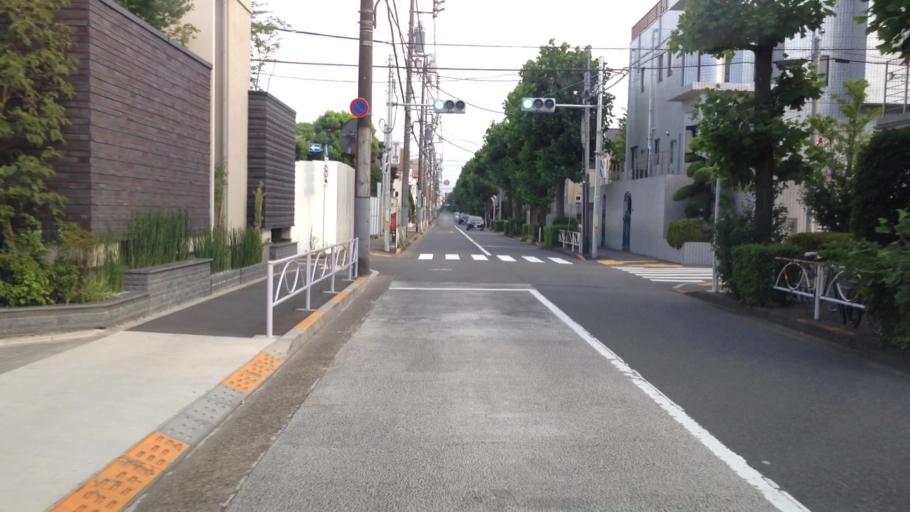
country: JP
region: Tokyo
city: Tokyo
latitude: 35.6251
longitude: 139.6727
